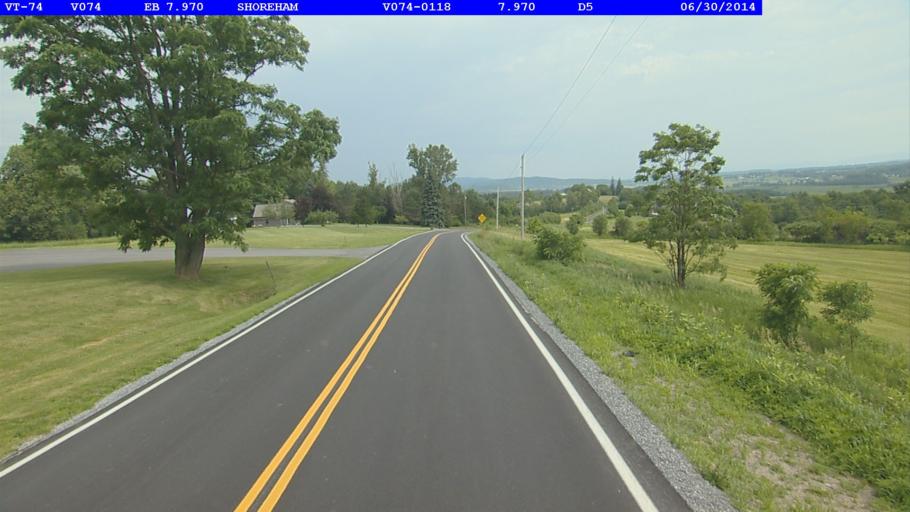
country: US
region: Vermont
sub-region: Addison County
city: Middlebury (village)
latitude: 43.9330
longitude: -73.2874
